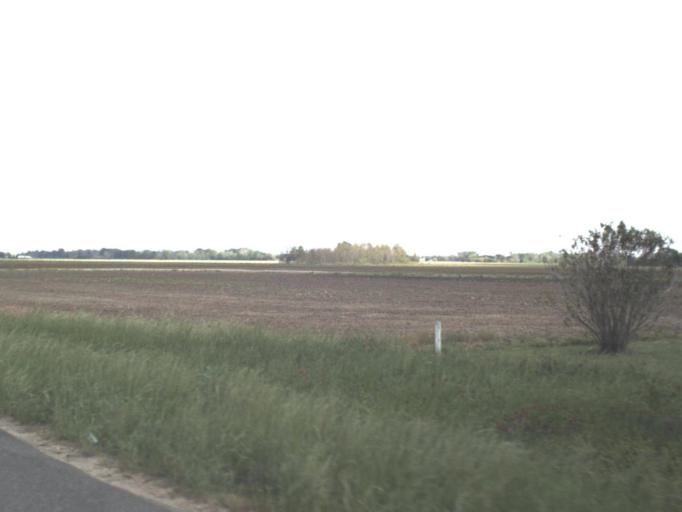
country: US
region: Florida
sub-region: Okaloosa County
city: Crestview
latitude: 30.8250
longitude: -86.6757
